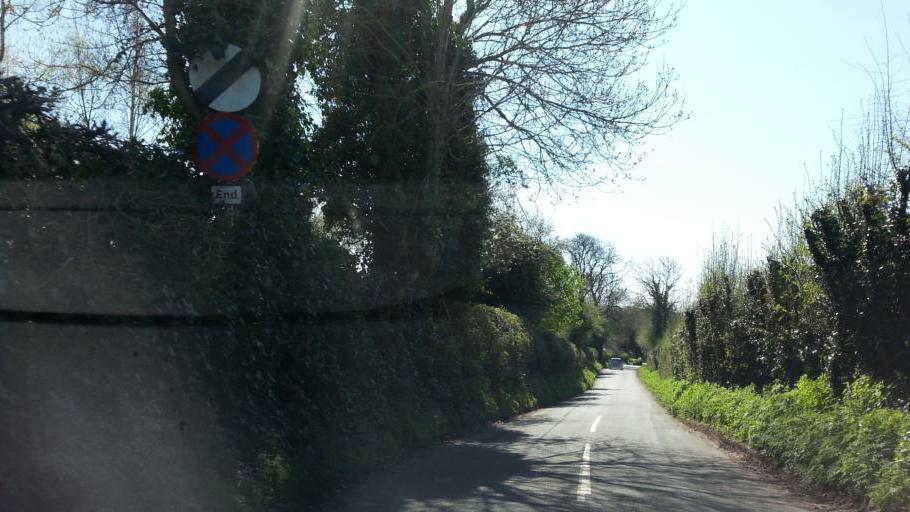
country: GB
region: England
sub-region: Staffordshire
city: Brewood
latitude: 52.6942
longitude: -2.1728
